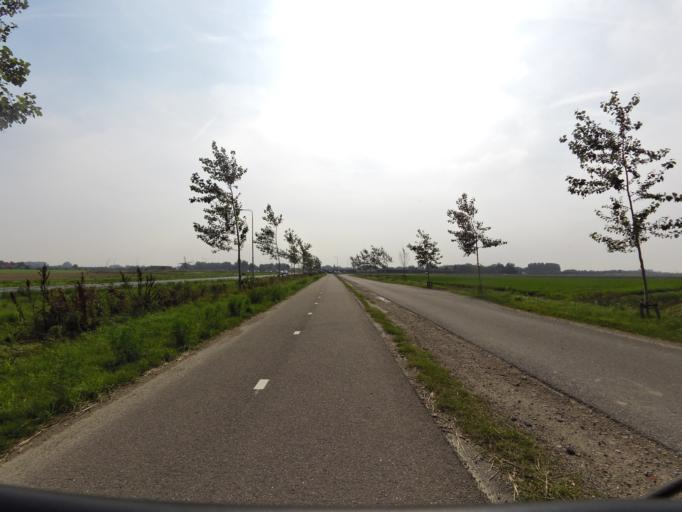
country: NL
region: Zeeland
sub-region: Gemeente Middelburg
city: Middelburg
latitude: 51.5596
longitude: 3.6000
